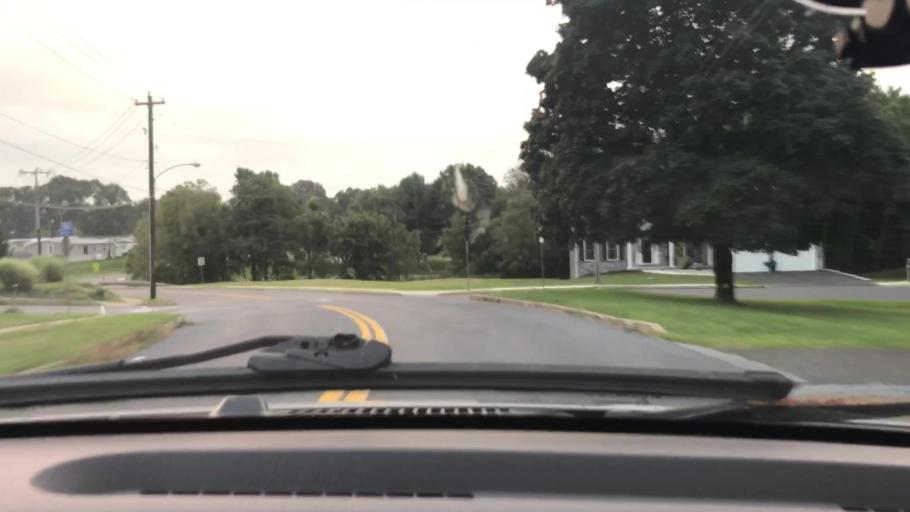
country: US
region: Pennsylvania
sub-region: Lancaster County
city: Elizabethtown
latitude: 40.1649
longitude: -76.5926
